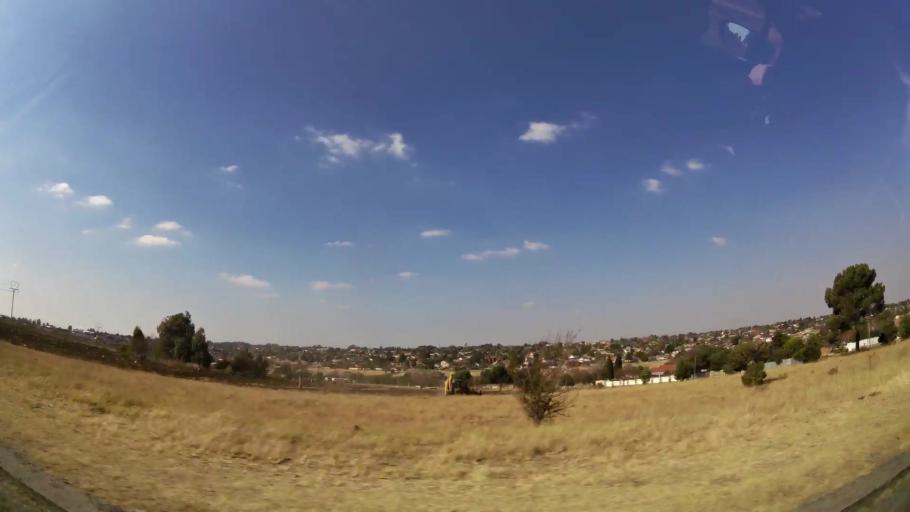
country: ZA
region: Gauteng
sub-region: City of Johannesburg Metropolitan Municipality
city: Roodepoort
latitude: -26.1364
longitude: 27.8189
